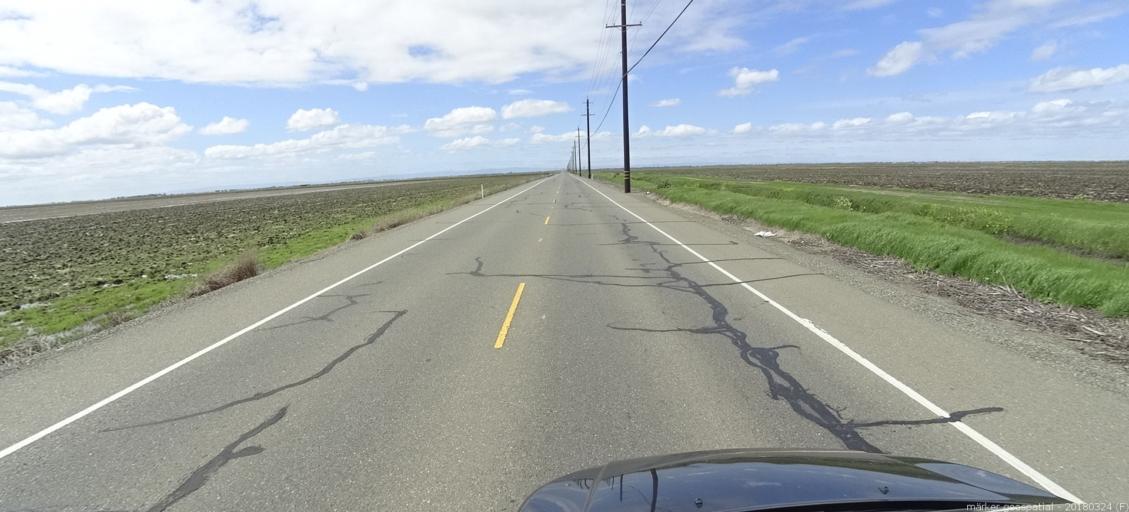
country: US
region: California
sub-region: Sacramento County
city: Elverta
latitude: 38.7143
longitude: -121.5130
